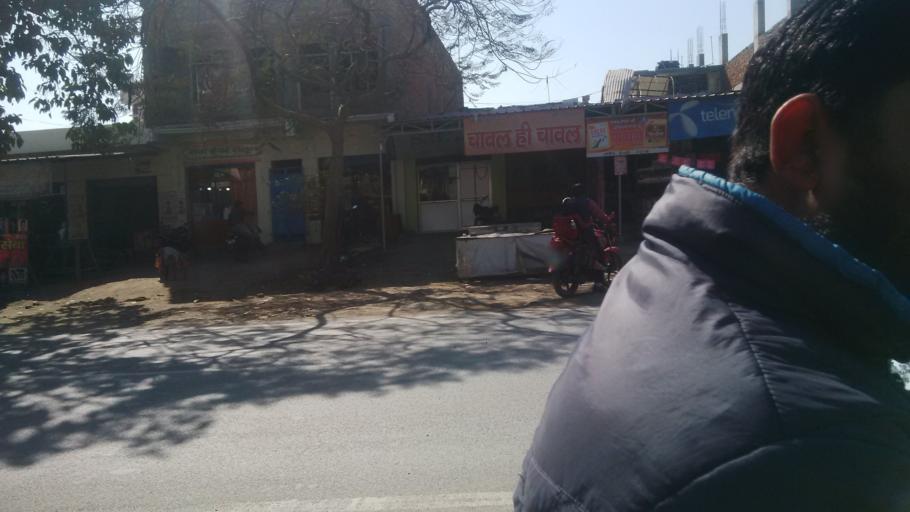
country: IN
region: Uttar Pradesh
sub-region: Rampur
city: Bilaspur
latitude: 29.0393
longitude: 79.2520
